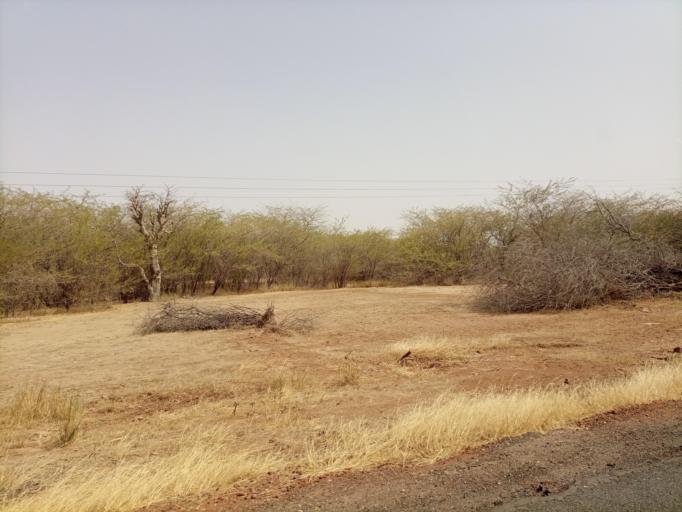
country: SN
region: Fatick
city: Foundiougne
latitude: 14.1875
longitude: -16.4539
